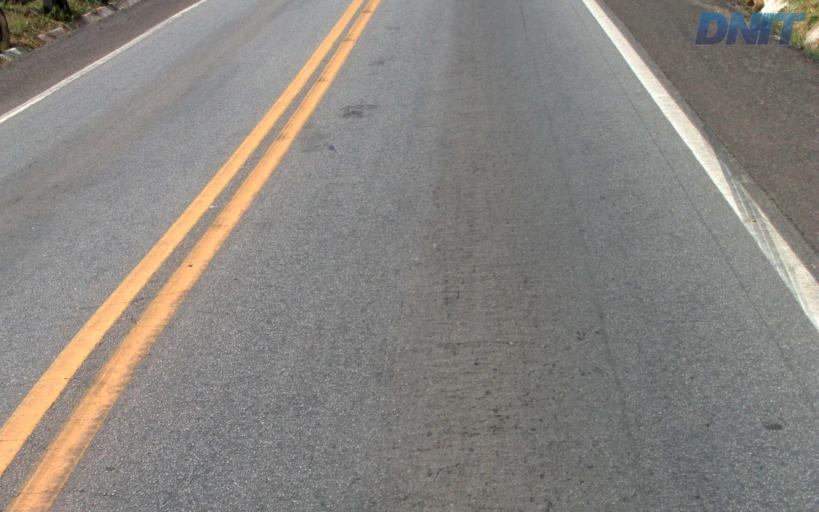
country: BR
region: Minas Gerais
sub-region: Ipatinga
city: Ipatinga
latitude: -19.4193
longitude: -42.4937
